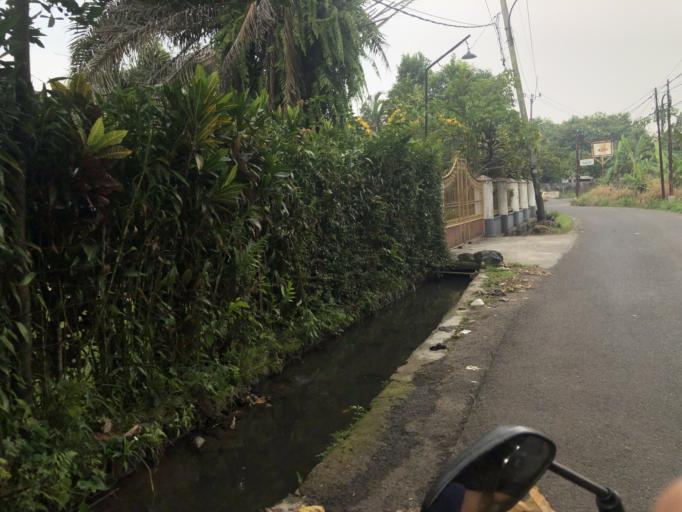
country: ID
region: West Java
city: Ciampea
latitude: -6.5686
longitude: 106.7466
